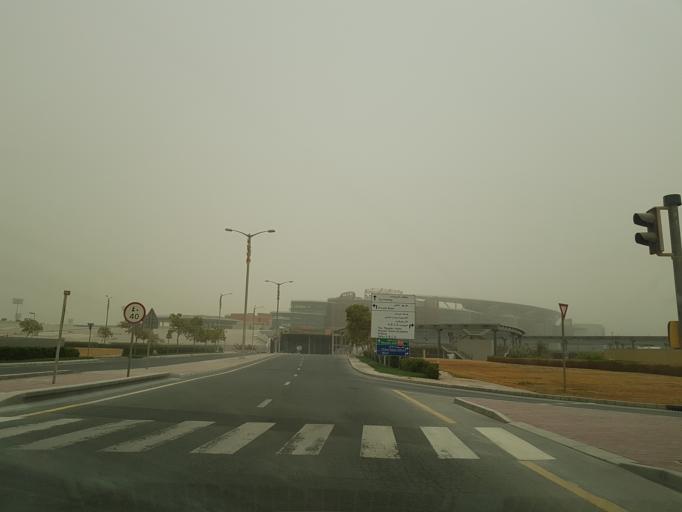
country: AE
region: Dubai
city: Dubai
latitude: 25.1637
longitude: 55.3033
